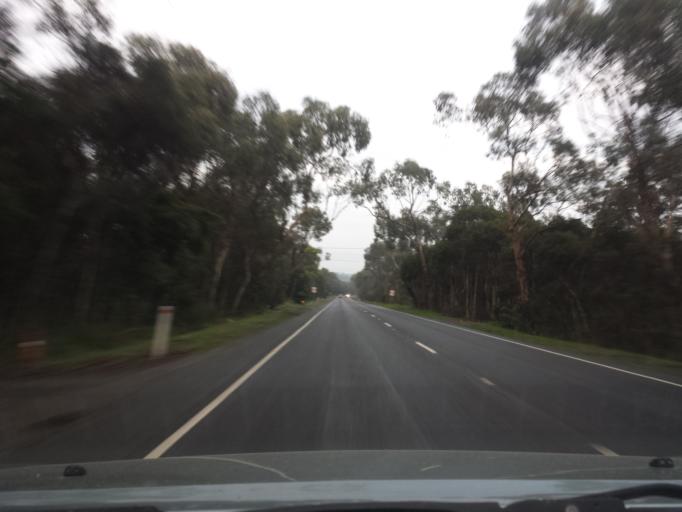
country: AU
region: Victoria
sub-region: Yarra Ranges
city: Belgrave South
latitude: -37.9582
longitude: 145.3458
